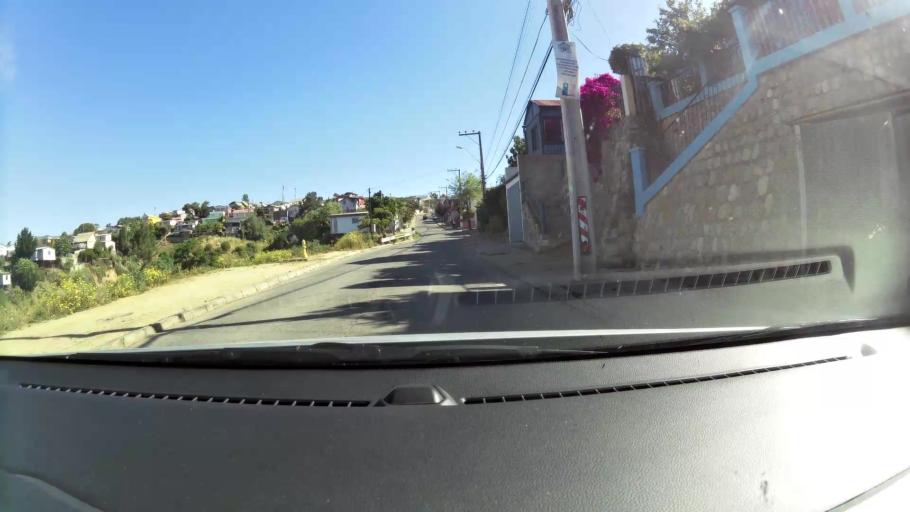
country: CL
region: Valparaiso
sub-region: Provincia de Valparaiso
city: Vina del Mar
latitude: -33.0419
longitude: -71.5621
